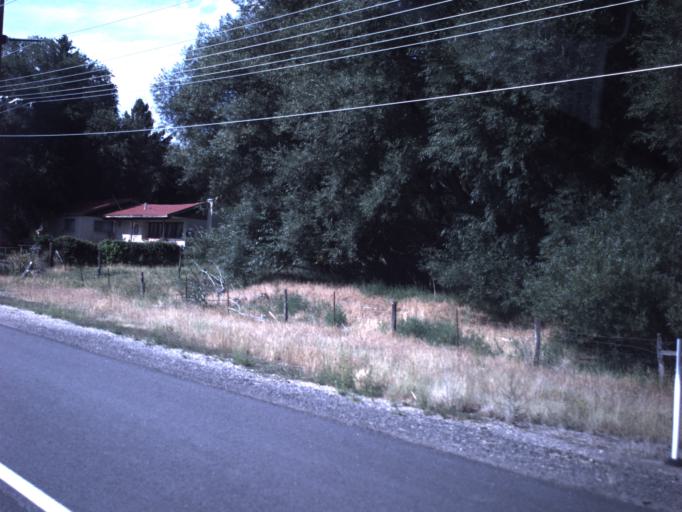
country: US
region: Utah
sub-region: Wasatch County
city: Heber
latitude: 40.5354
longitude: -111.4101
